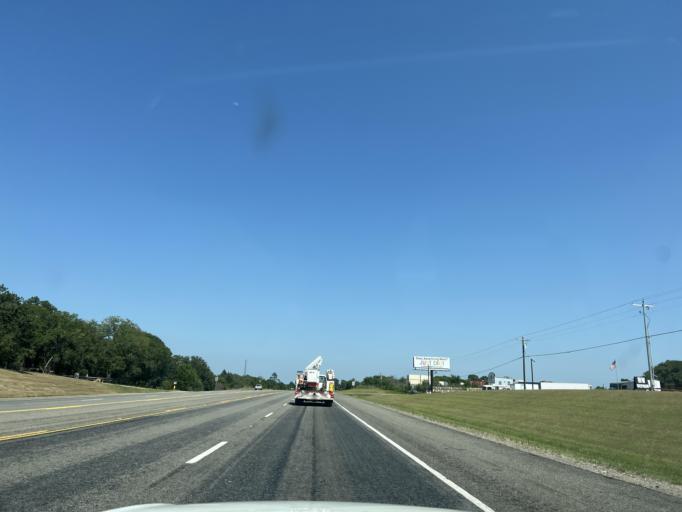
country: US
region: Texas
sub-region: Washington County
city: Brenham
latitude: 30.1732
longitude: -96.4521
